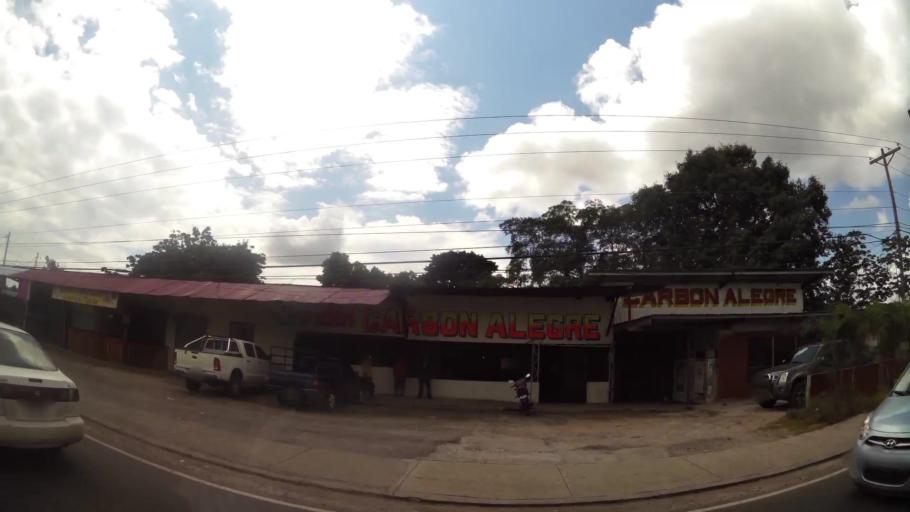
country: PA
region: Panama
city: Nuevo Arraijan
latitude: 8.9254
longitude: -79.7124
